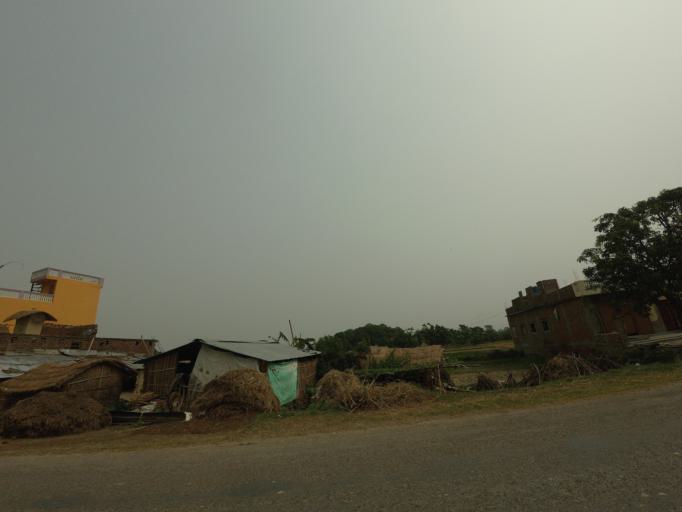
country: IN
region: Uttar Pradesh
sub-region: Maharajganj
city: Nautanwa
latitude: 27.4933
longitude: 83.3216
